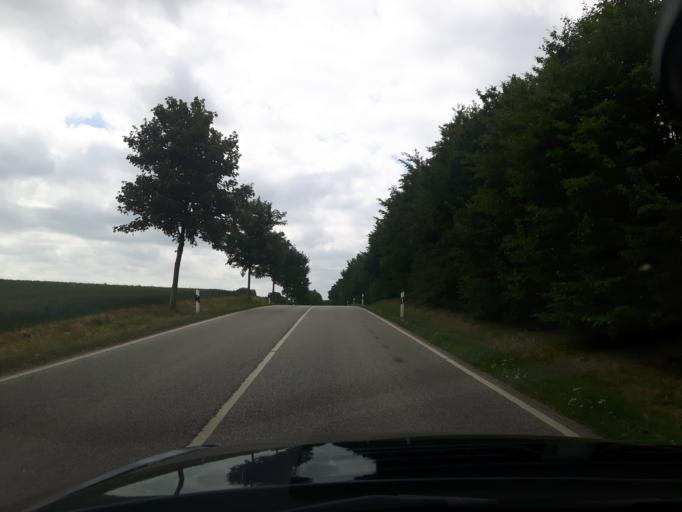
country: DE
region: Schleswig-Holstein
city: Altenkrempe
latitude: 54.0994
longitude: 10.8530
